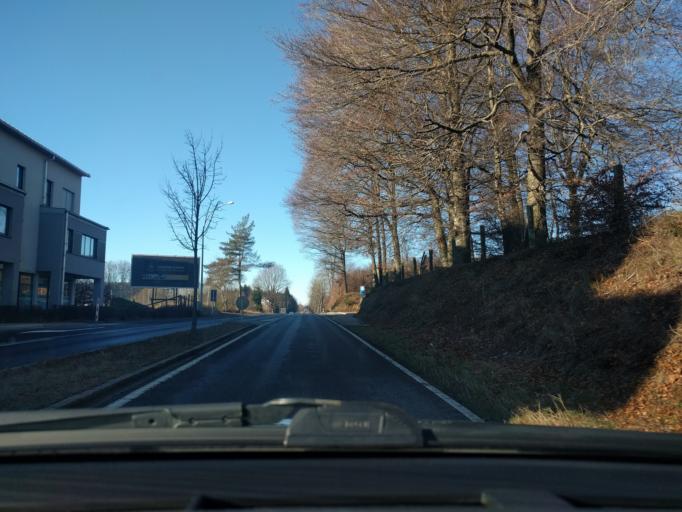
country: LU
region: Diekirch
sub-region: Canton de Clervaux
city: Weiswampach
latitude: 50.1569
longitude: 6.0492
